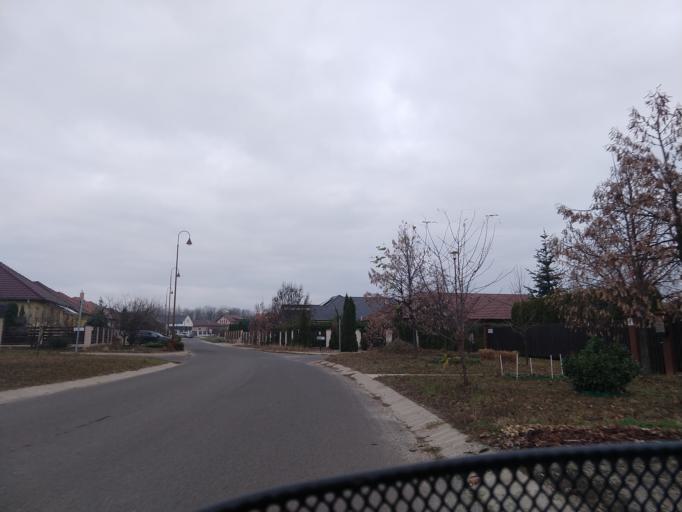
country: HU
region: Pest
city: Orbottyan
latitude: 47.6601
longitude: 19.2549
